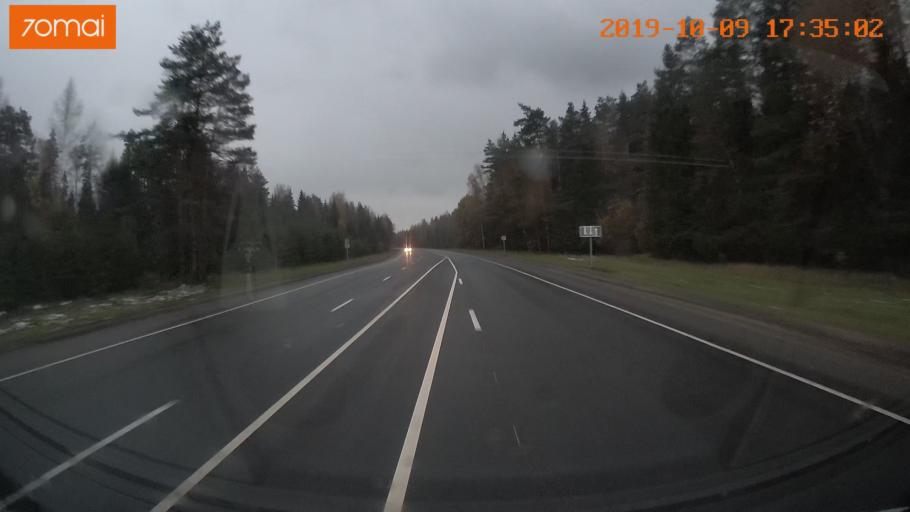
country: RU
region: Ivanovo
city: Bogorodskoye
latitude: 57.0996
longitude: 41.0056
